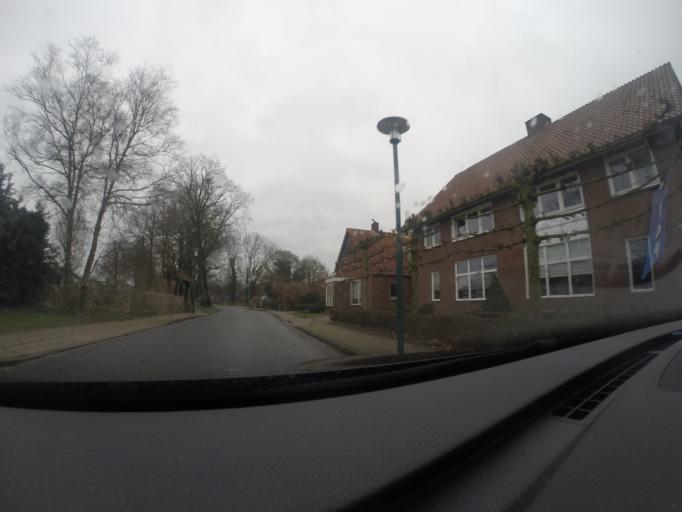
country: NL
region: Overijssel
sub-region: Gemeente Hengelo
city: Hengelo
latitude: 52.2041
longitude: 6.7912
